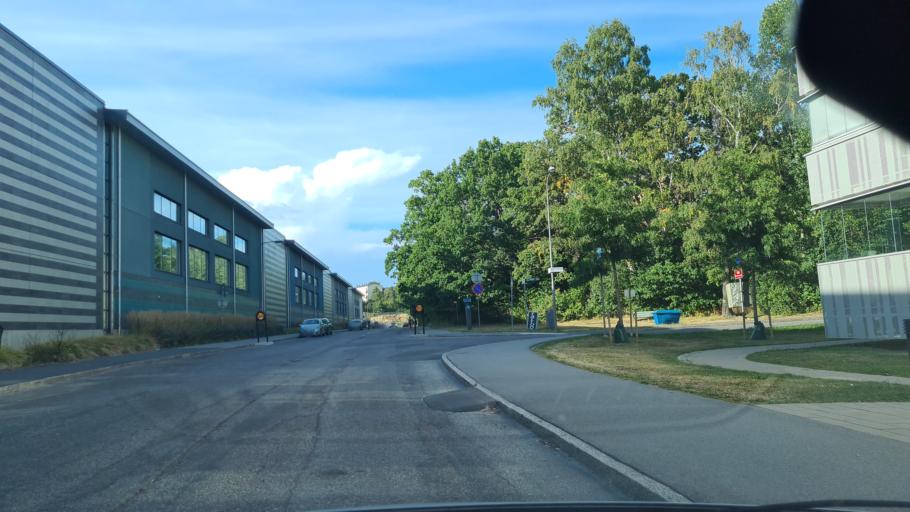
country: SE
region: Stockholm
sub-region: Stockholms Kommun
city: Arsta
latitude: 59.2913
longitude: 18.0957
